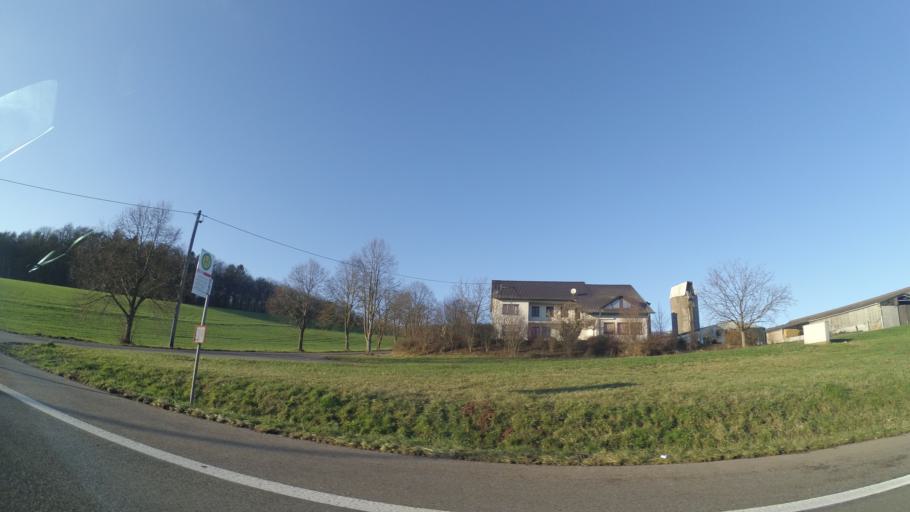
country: DE
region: Saarland
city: Saarwellingen
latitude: 49.3541
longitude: 6.8524
